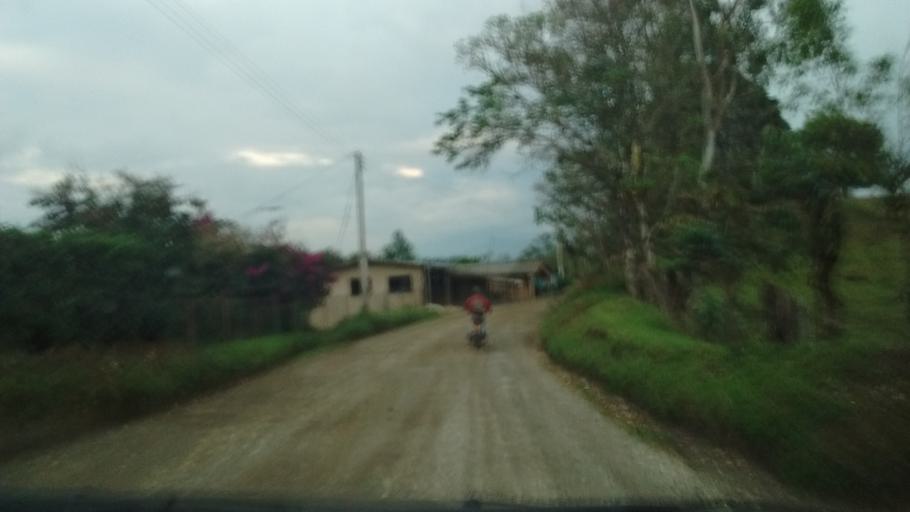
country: CO
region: Cauca
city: Lopez
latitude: 2.3880
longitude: -76.7311
